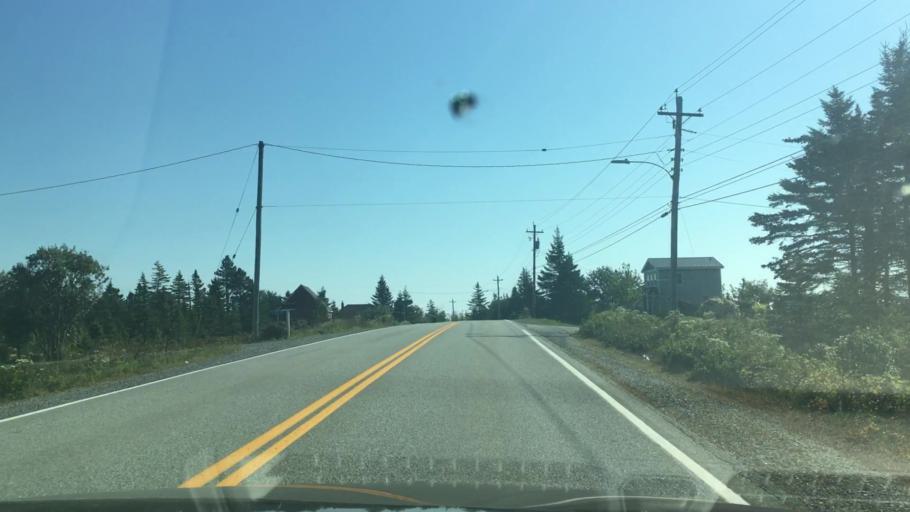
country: CA
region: Nova Scotia
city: Cole Harbour
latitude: 44.7788
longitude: -62.7800
